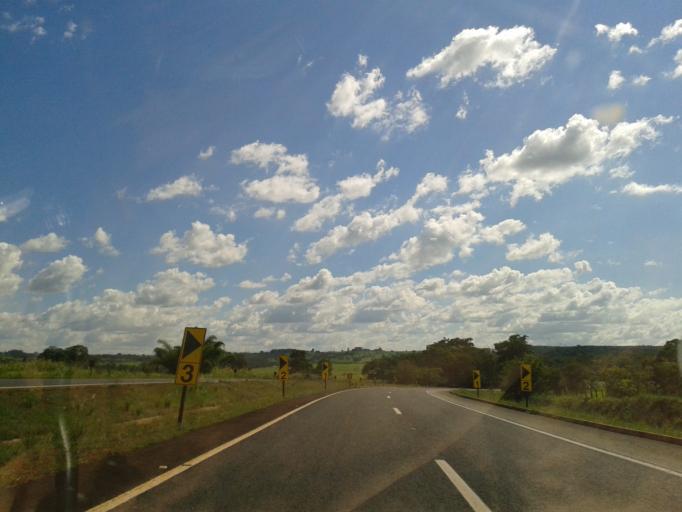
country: BR
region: Goias
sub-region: Morrinhos
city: Morrinhos
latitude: -17.7803
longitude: -49.1796
